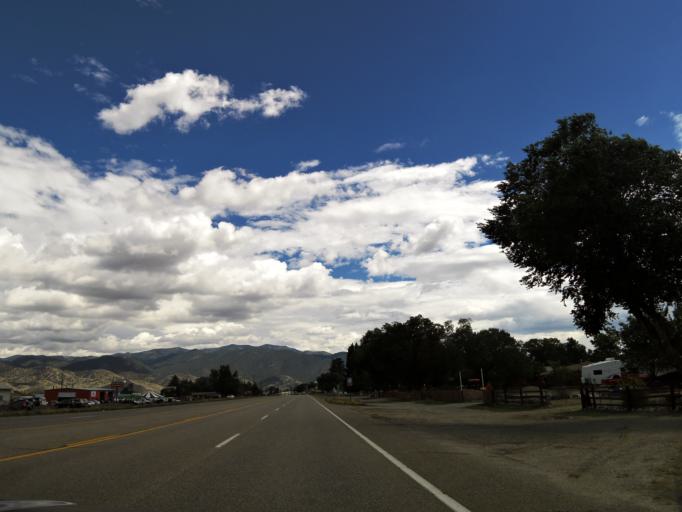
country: US
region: Colorado
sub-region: Chaffee County
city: Salida
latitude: 38.5217
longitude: -106.0295
